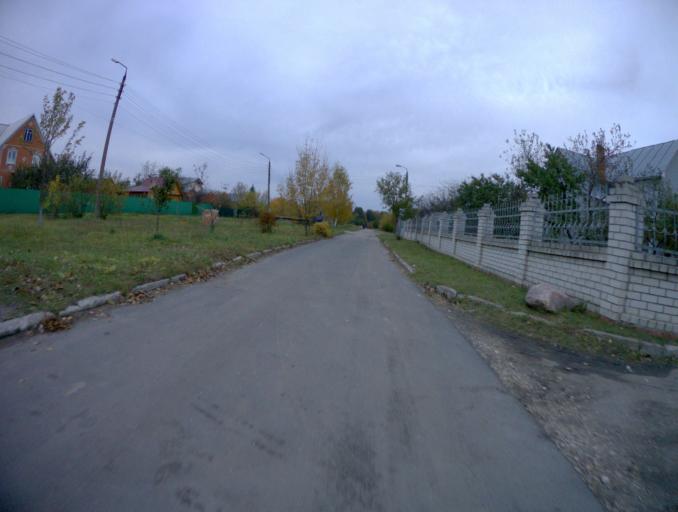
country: RU
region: Vladimir
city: Kommunar
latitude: 56.0585
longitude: 40.4939
